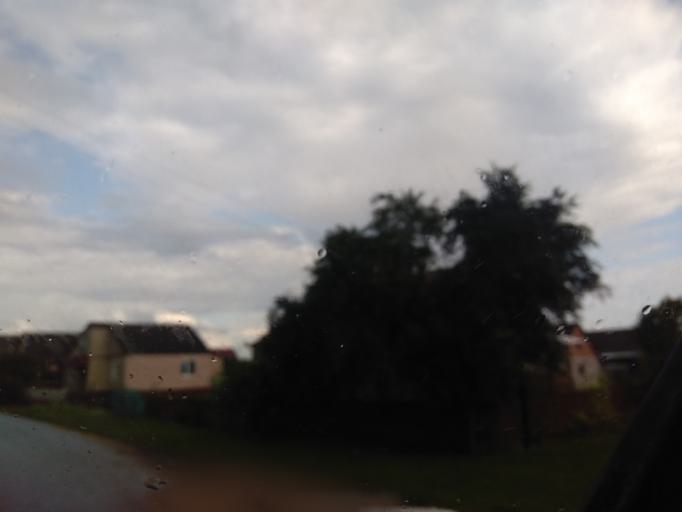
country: BY
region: Minsk
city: Kapyl'
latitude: 53.1442
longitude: 27.1119
